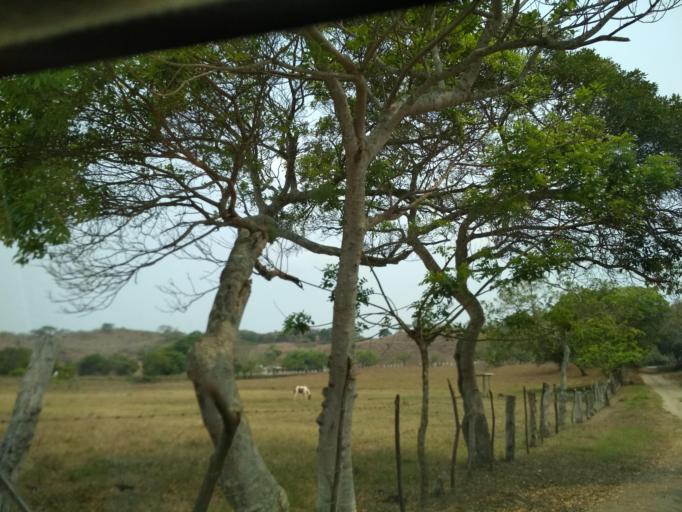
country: MX
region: Veracruz
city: Anton Lizardo
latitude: 19.0170
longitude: -95.9885
